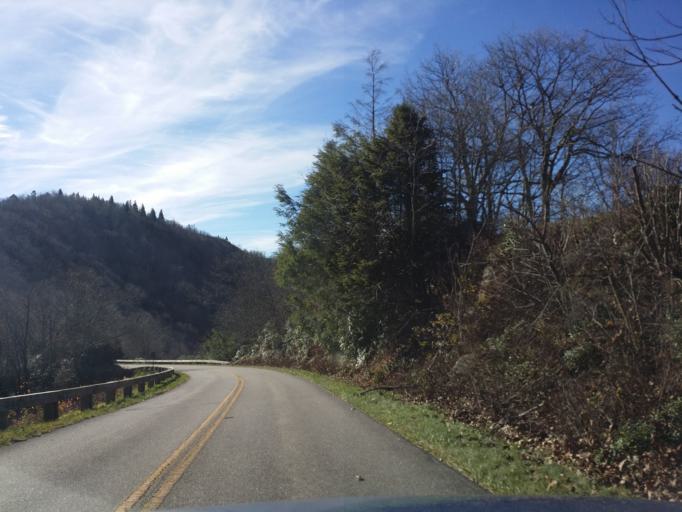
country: US
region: North Carolina
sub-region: Buncombe County
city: Black Mountain
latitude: 35.7230
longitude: -82.2186
